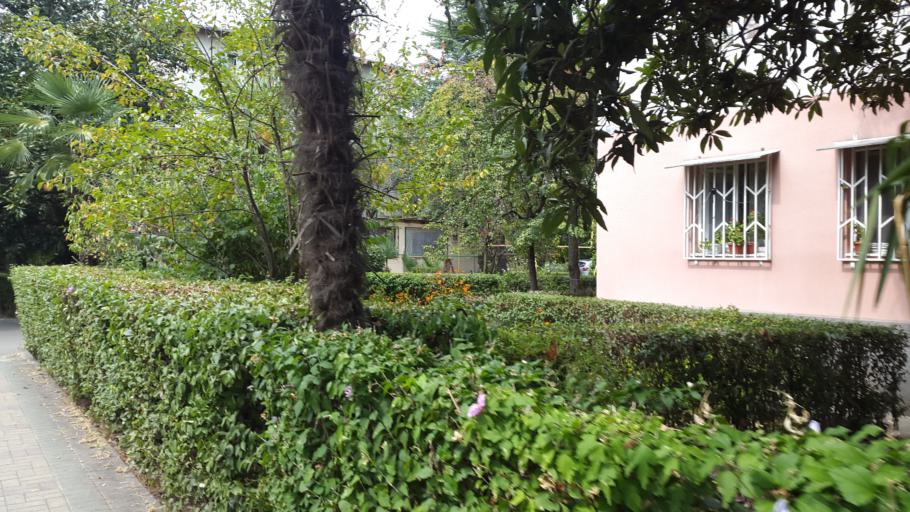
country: RU
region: Krasnodarskiy
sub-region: Sochi City
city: Sochi
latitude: 43.6023
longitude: 39.7254
